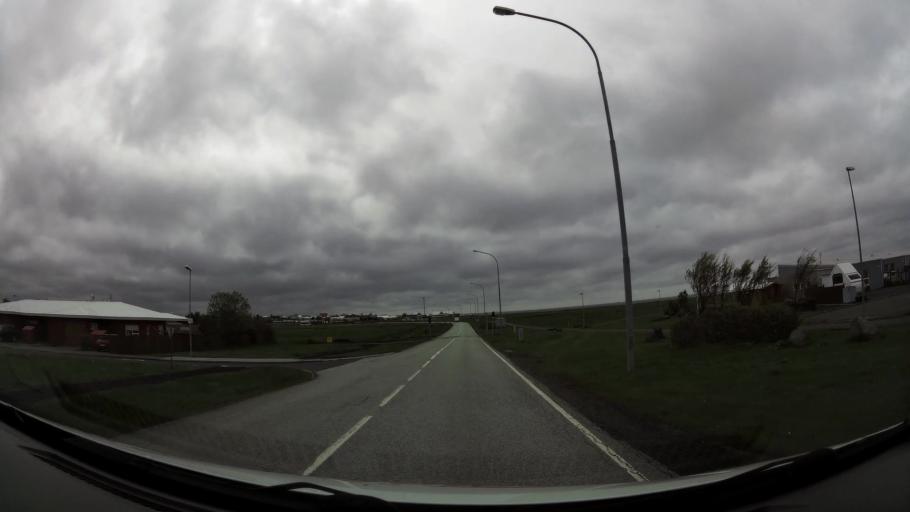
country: IS
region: Capital Region
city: Alftanes
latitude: 64.1081
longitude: -22.0216
